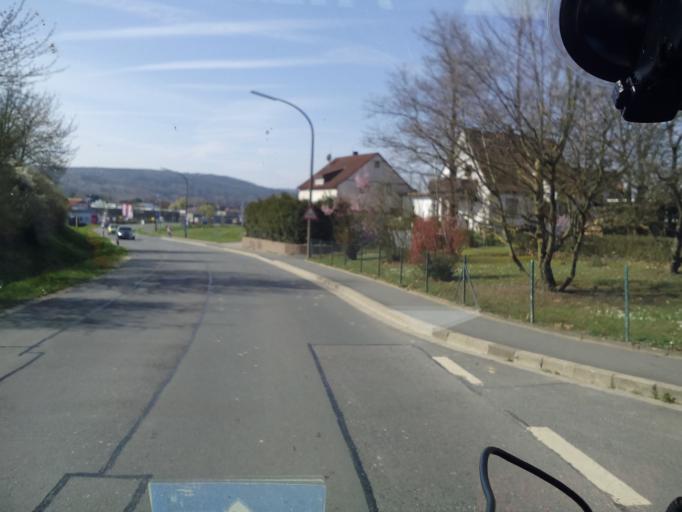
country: DE
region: Bavaria
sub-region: Upper Franconia
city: Michelau
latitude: 50.1732
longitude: 11.1199
